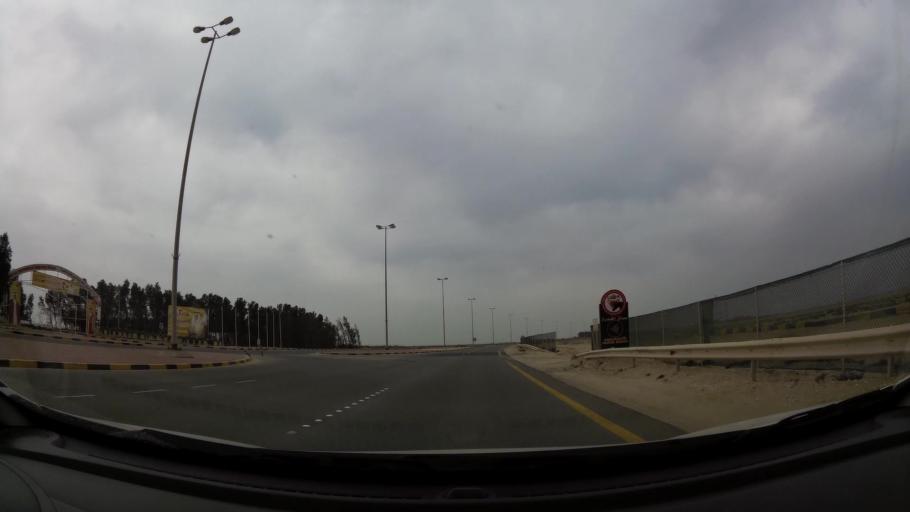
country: BH
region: Central Governorate
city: Dar Kulayb
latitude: 25.9932
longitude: 50.4790
